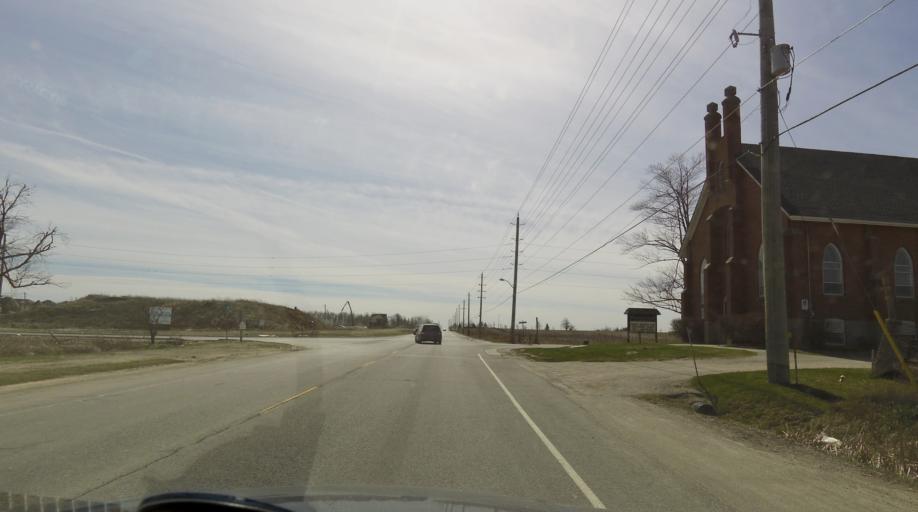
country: CA
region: Ontario
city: Brampton
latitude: 43.7050
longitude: -79.8566
